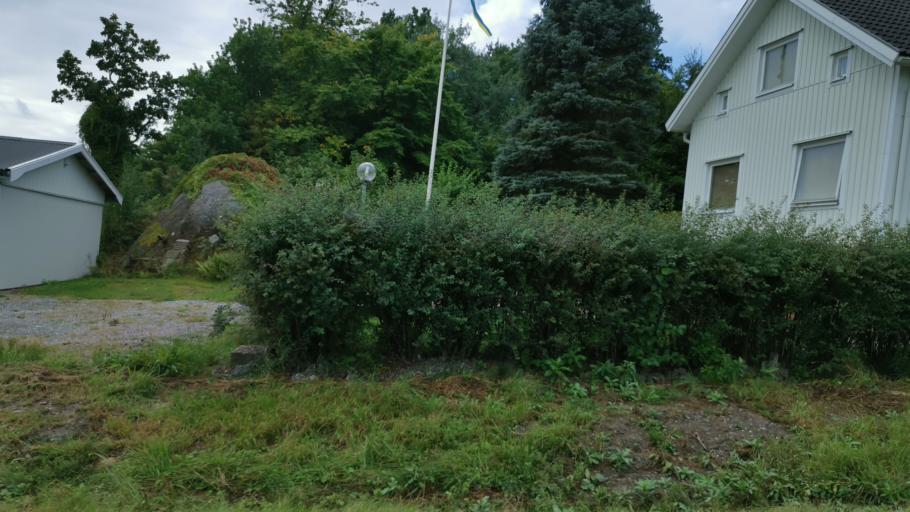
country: SE
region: Vaestra Goetaland
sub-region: Sotenas Kommun
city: Hunnebostrand
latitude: 58.5065
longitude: 11.3195
